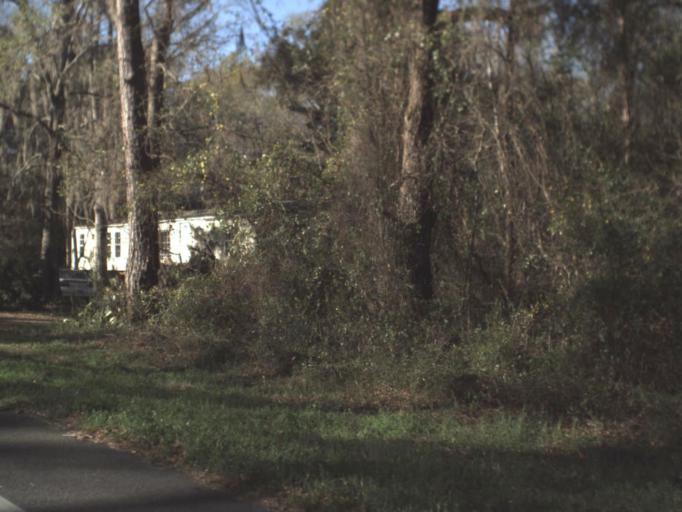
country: US
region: Georgia
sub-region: Brooks County
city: Quitman
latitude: 30.5771
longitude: -83.6370
